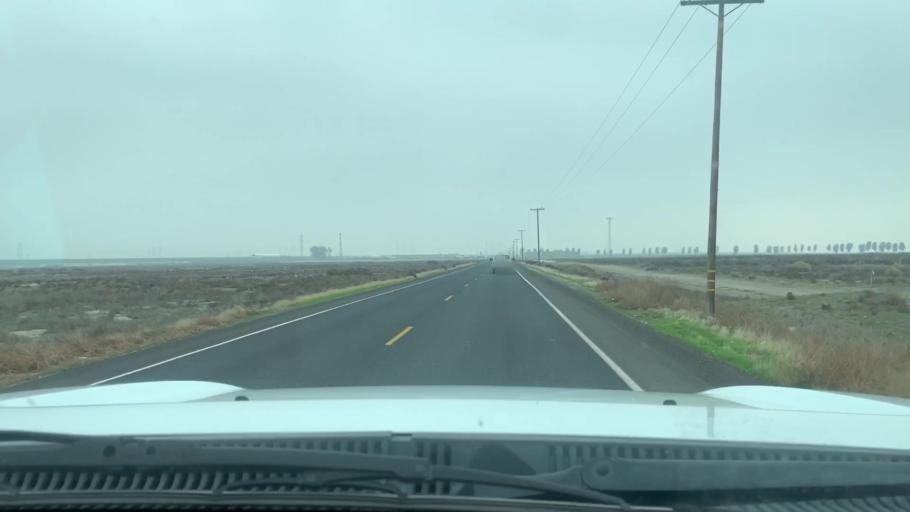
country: US
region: California
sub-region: Kern County
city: Buttonwillow
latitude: 35.4996
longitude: -119.5594
